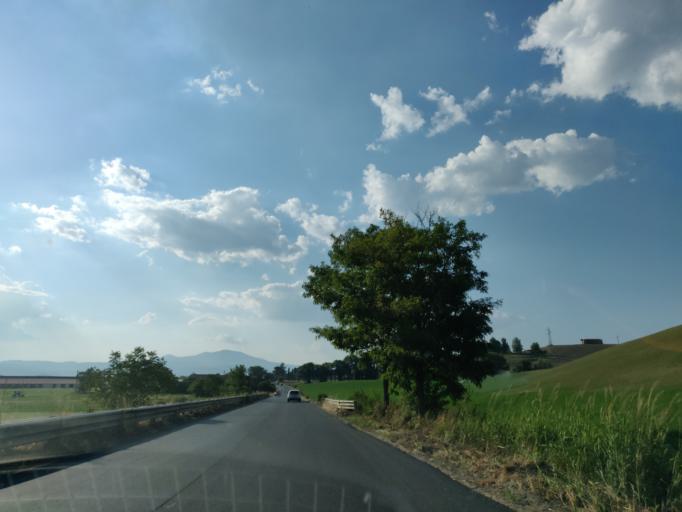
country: IT
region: Latium
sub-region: Provincia di Viterbo
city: Proceno
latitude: 42.7841
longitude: 11.8315
